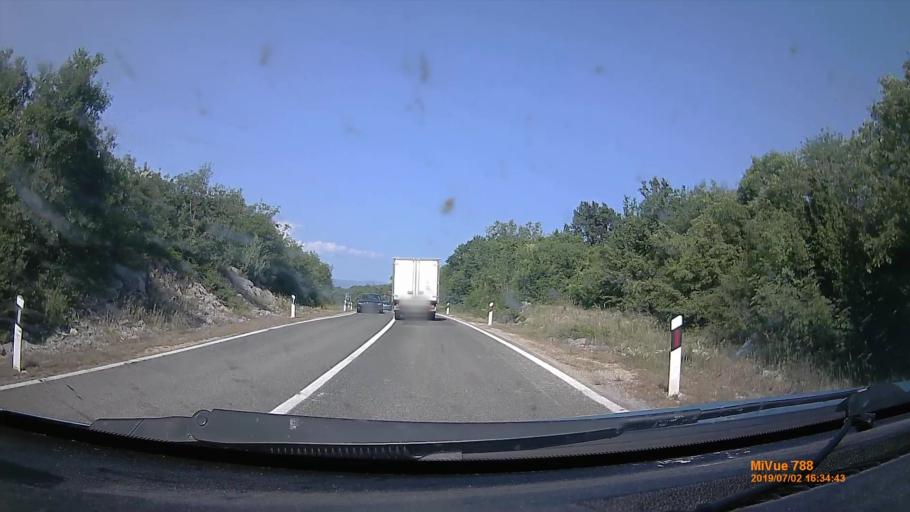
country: HR
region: Primorsko-Goranska
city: Njivice
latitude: 45.0829
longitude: 14.5059
